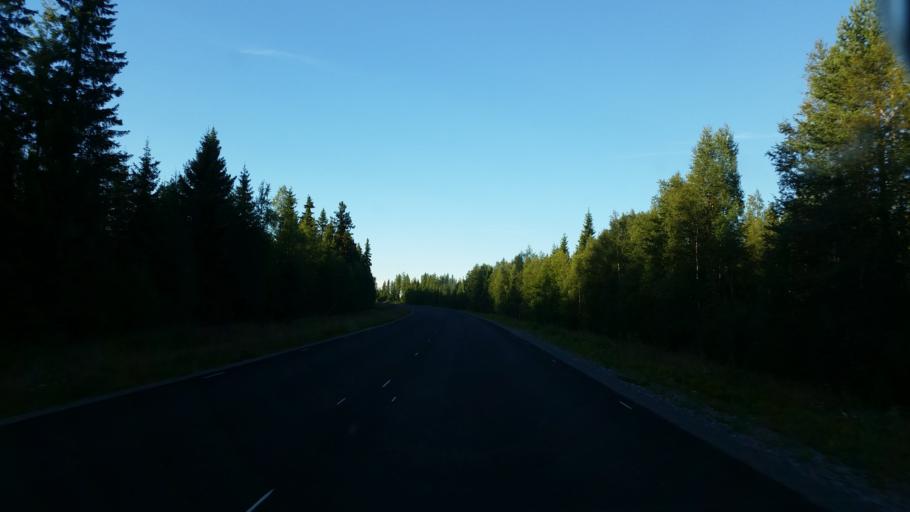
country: SE
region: Vaesterbotten
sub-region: Dorotea Kommun
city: Dorotea
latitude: 64.3094
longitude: 16.6015
